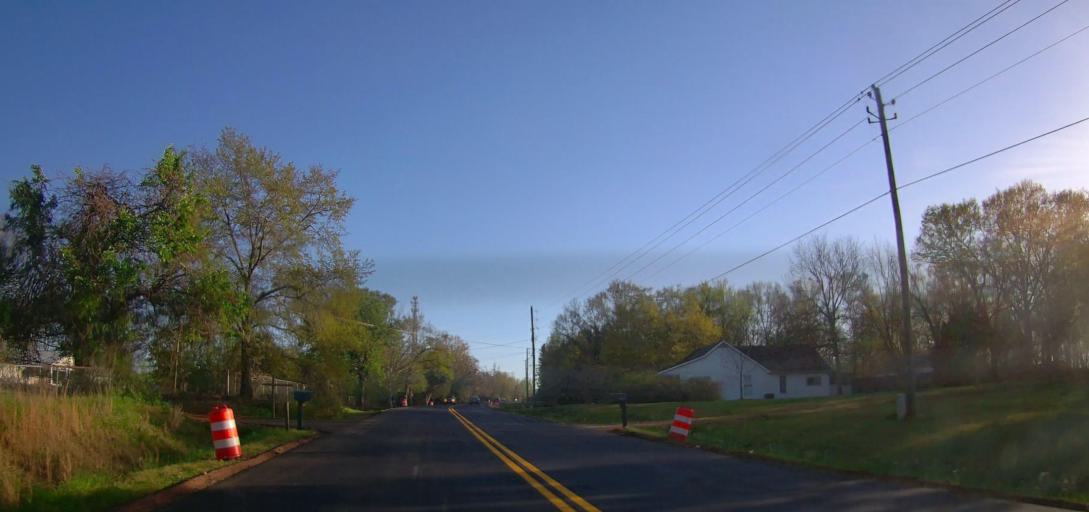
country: US
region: Georgia
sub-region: Newton County
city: Porterdale
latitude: 33.5506
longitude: -83.9117
